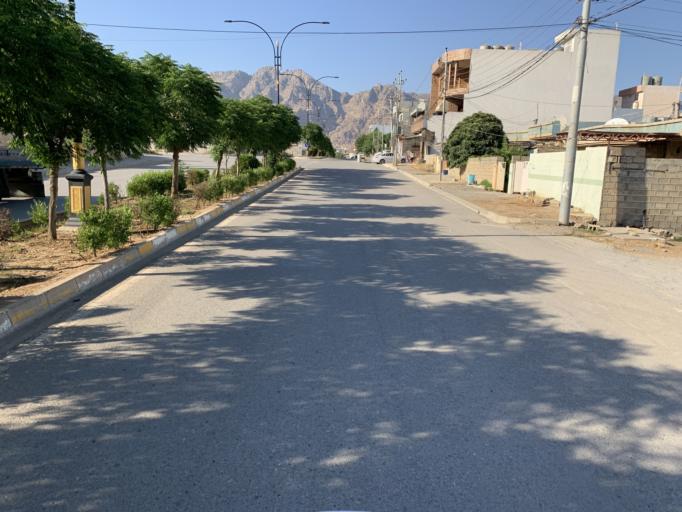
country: IQ
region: As Sulaymaniyah
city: Raniye
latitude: 36.2443
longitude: 44.8734
